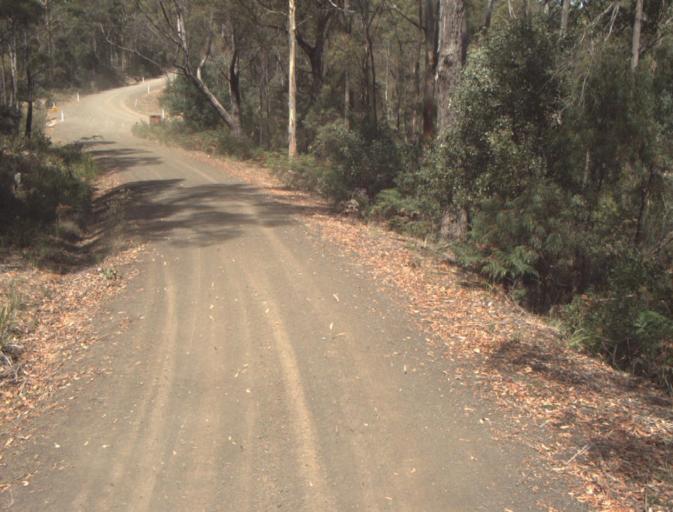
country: AU
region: Tasmania
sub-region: Launceston
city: Mayfield
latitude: -41.2776
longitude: 147.1158
